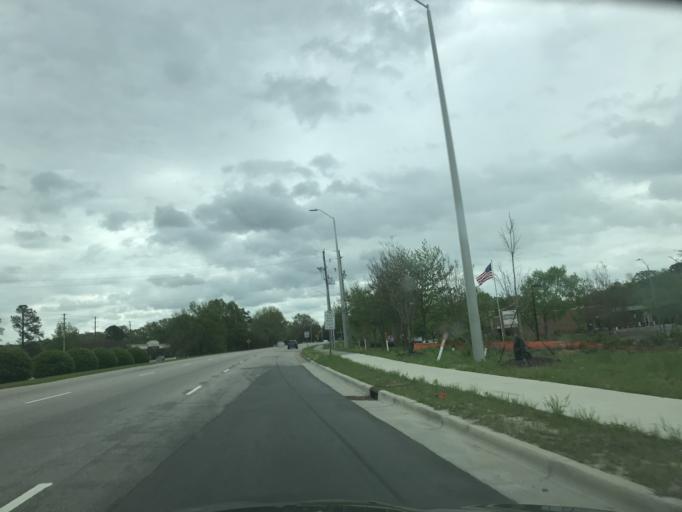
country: US
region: North Carolina
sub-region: Wake County
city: Knightdale
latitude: 35.7984
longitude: -78.4985
